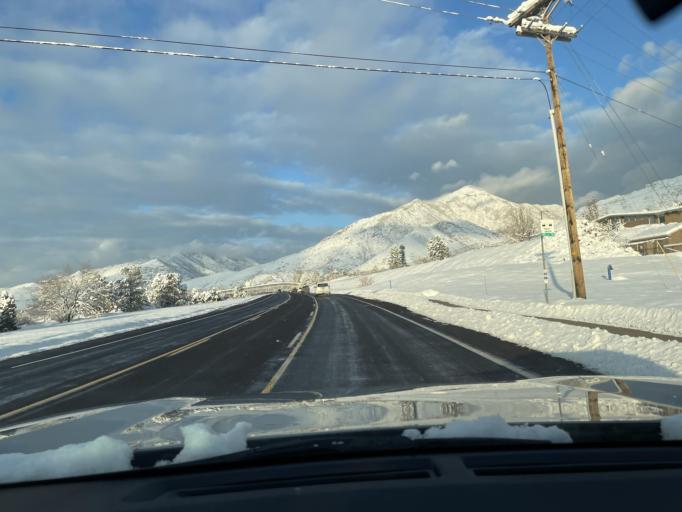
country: US
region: Utah
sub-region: Salt Lake County
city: Mount Olympus
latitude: 40.6746
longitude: -111.8011
